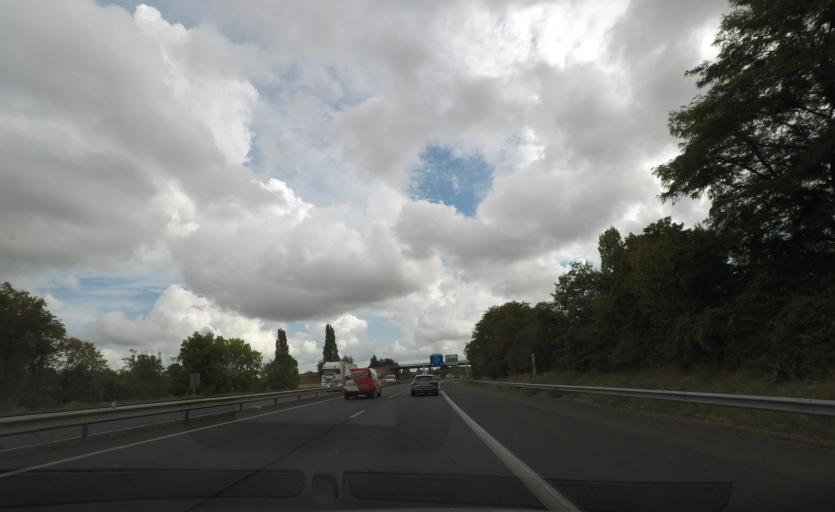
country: FR
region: Pays de la Loire
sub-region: Departement de Maine-et-Loire
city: Pellouailles-les-Vignes
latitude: 47.5163
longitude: -0.4373
